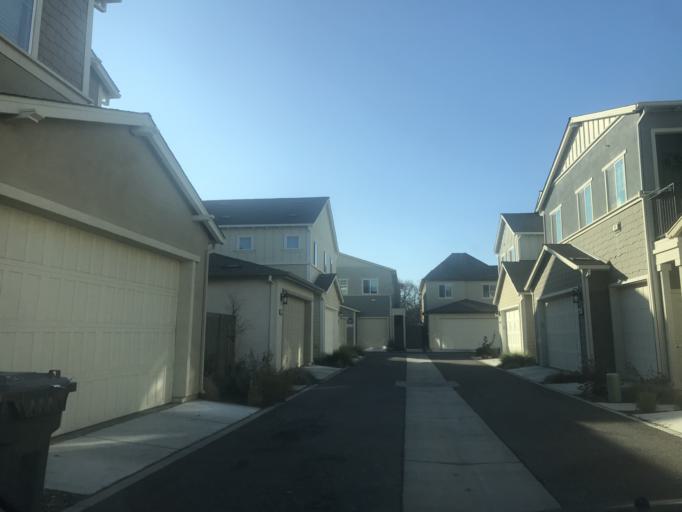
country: US
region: California
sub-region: Yolo County
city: Davis
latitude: 38.5664
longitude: -121.7434
